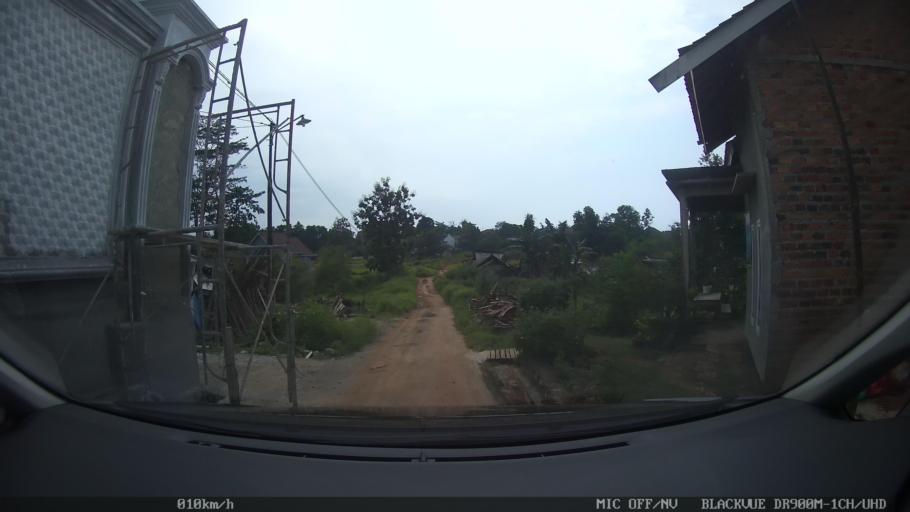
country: ID
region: Lampung
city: Kedaton
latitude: -5.3511
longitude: 105.2441
